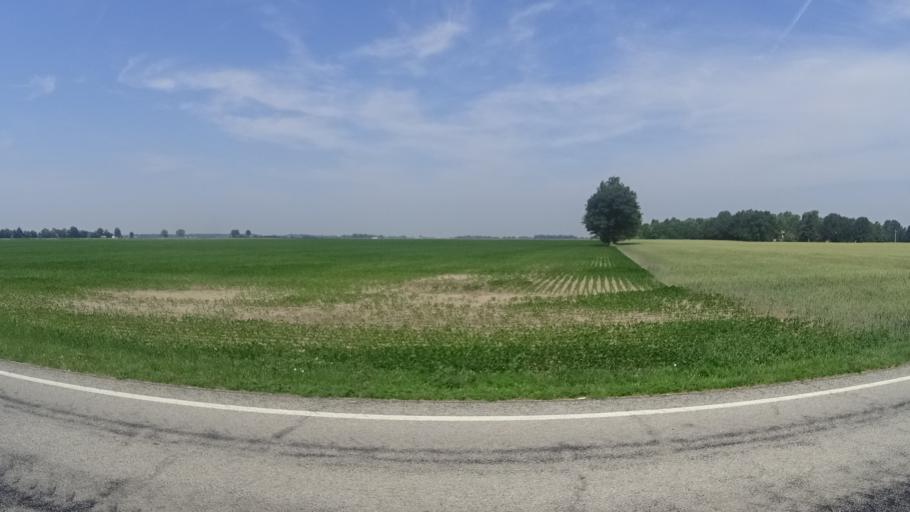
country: US
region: Ohio
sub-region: Huron County
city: Monroeville
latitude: 41.3117
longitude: -82.7142
